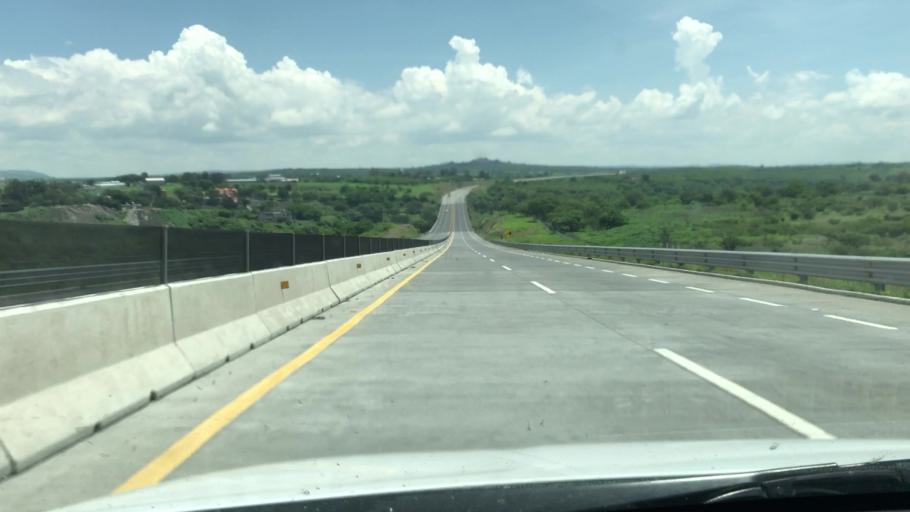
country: MX
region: Jalisco
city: Degollado
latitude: 20.3740
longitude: -102.1246
